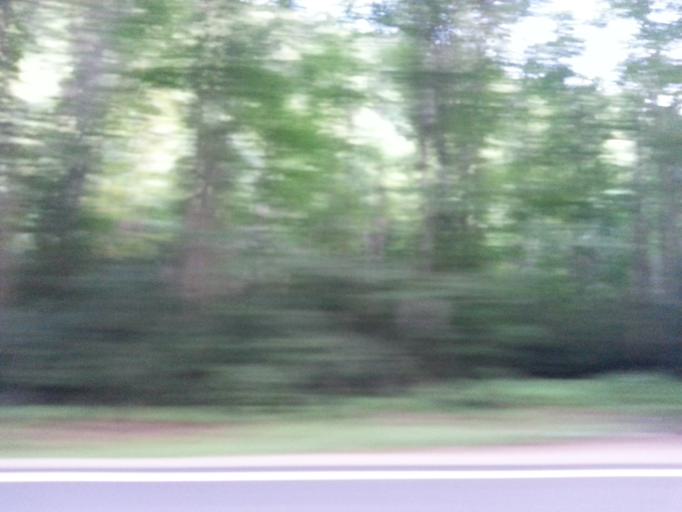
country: US
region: Tennessee
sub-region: Johnson County
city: Mountain City
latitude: 36.5915
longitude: -81.8194
